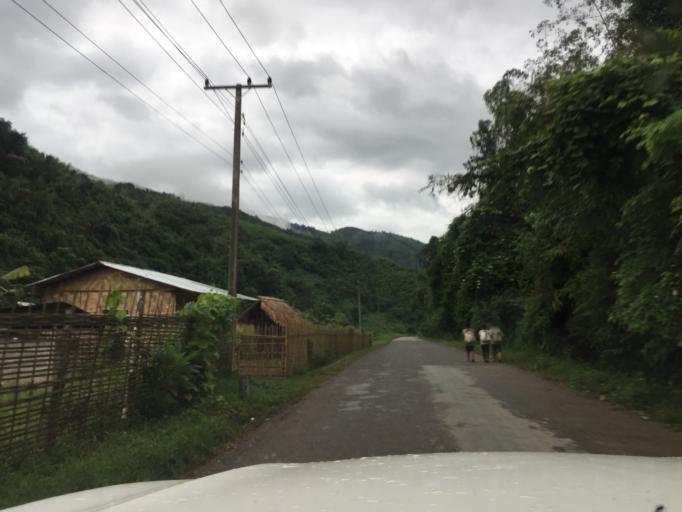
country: LA
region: Oudomxai
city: Muang La
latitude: 20.9761
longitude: 102.2237
